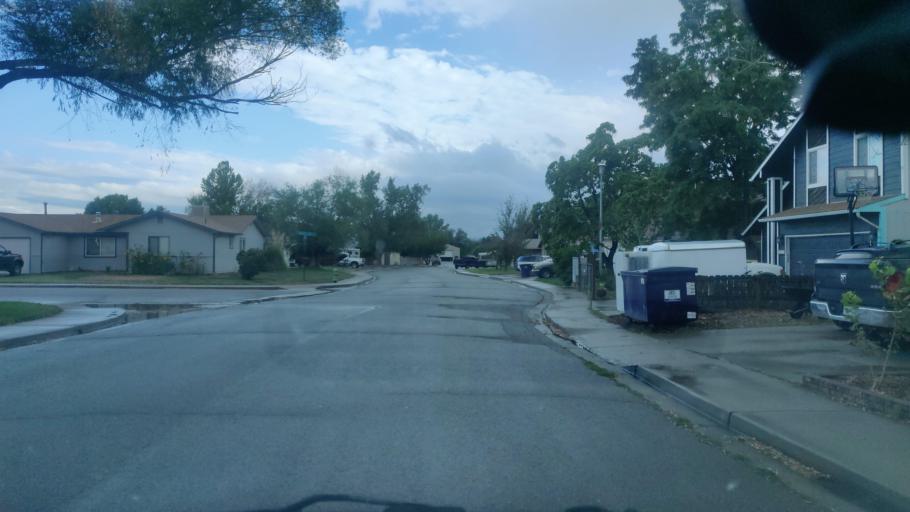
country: US
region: Colorado
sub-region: Mesa County
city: Fruitvale
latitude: 39.0718
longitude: -108.4850
